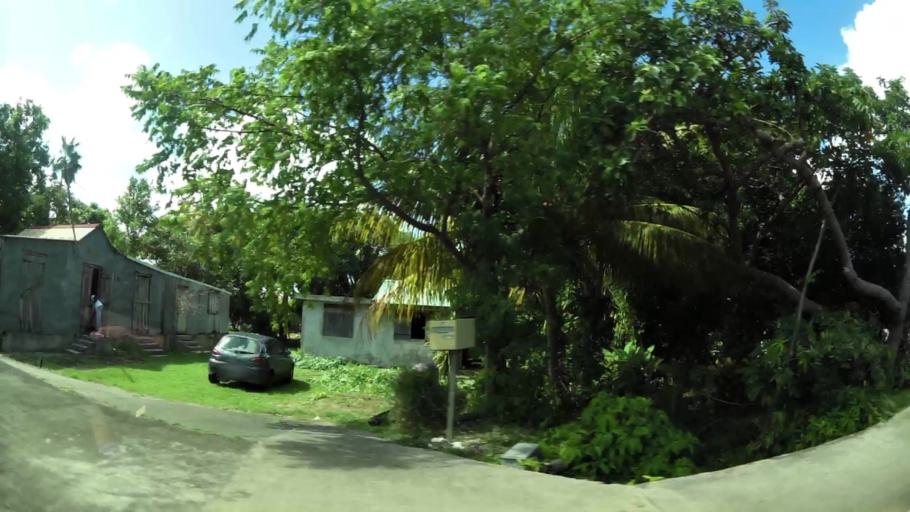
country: GP
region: Guadeloupe
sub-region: Guadeloupe
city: Anse-Bertrand
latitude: 16.4407
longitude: -61.4748
